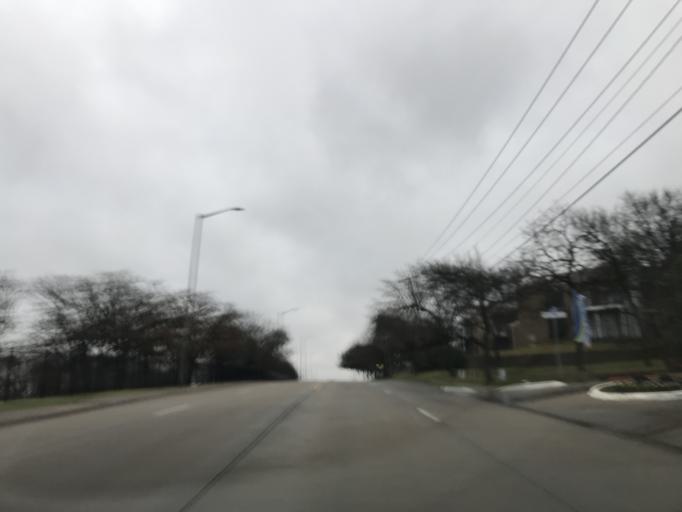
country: US
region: Texas
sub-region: Tarrant County
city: Arlington
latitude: 32.7754
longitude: -97.1004
